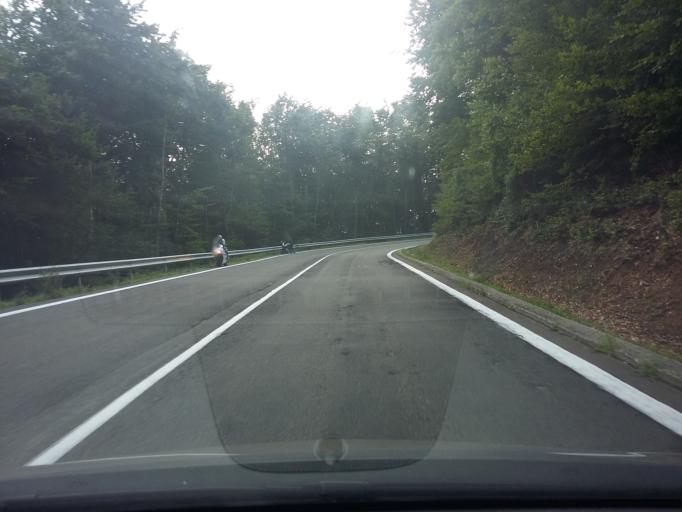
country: SK
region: Bratislavsky
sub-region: Okres Pezinok
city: Pezinok
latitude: 48.3504
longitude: 17.2144
